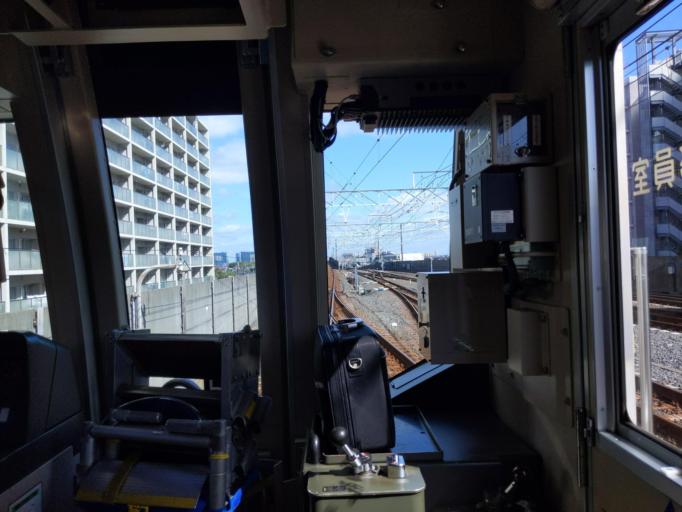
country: JP
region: Chiba
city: Shiroi
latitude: 35.7291
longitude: 140.0749
